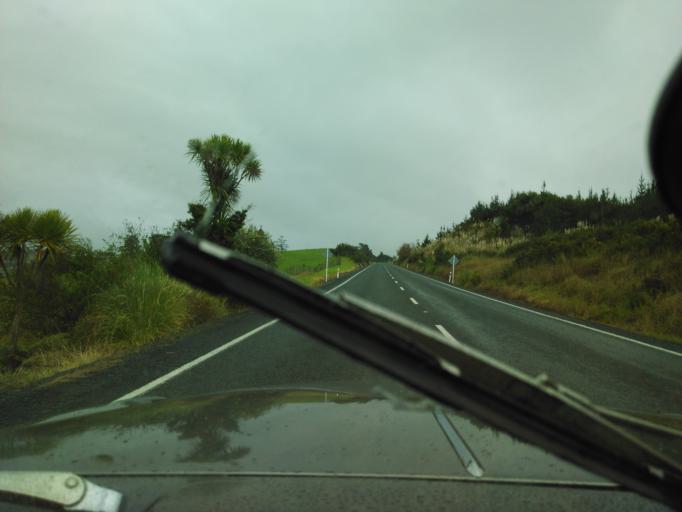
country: NZ
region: Auckland
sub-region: Auckland
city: Wellsford
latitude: -36.3274
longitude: 174.4714
